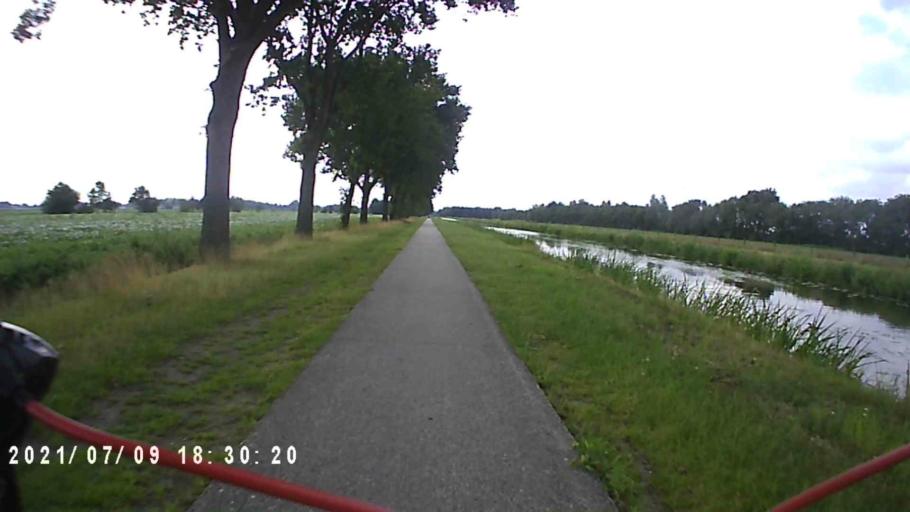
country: NL
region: Groningen
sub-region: Gemeente Pekela
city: Oude Pekela
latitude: 53.0651
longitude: 6.9766
